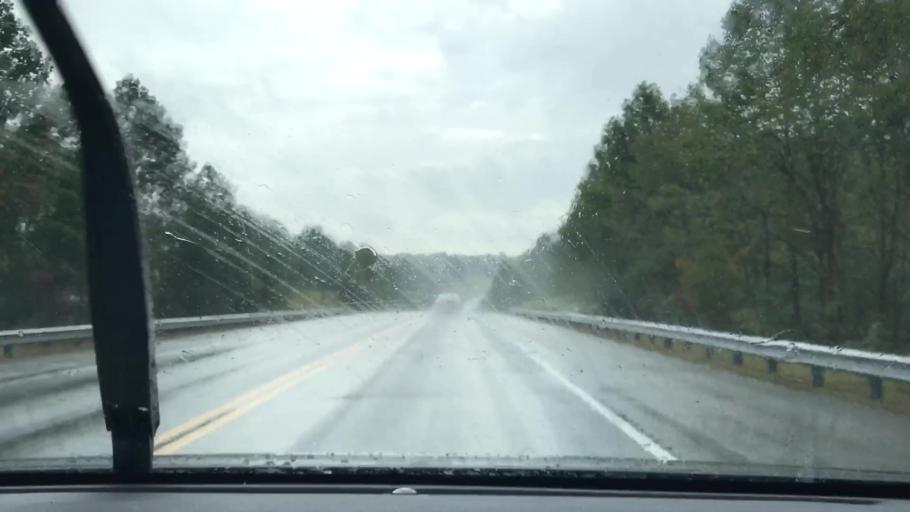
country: US
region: Tennessee
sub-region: Macon County
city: Lafayette
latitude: 36.5319
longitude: -86.0957
